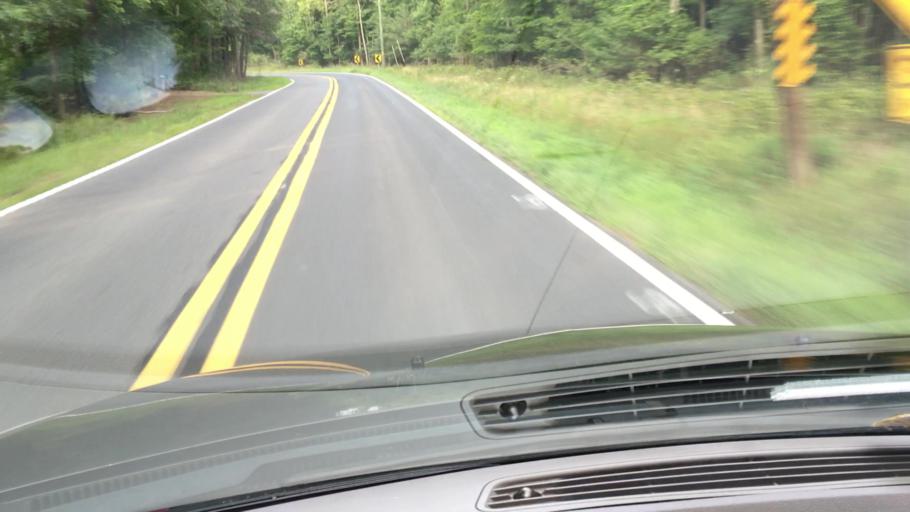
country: US
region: Delaware
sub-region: Sussex County
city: Ocean View
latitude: 38.5075
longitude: -75.1148
